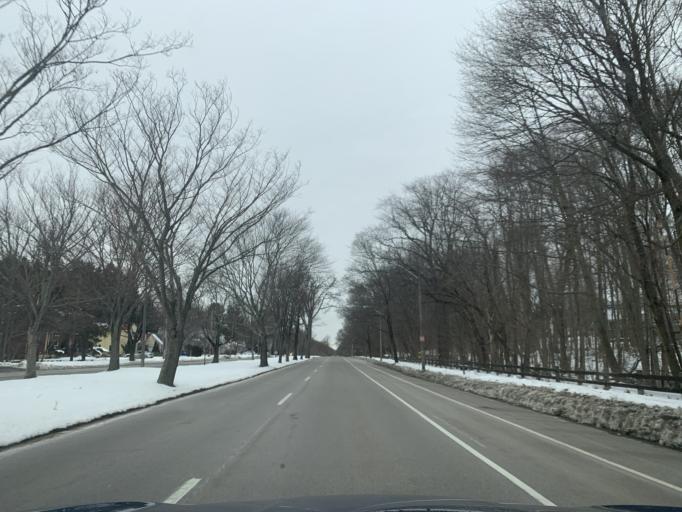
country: US
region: Massachusetts
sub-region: Norfolk County
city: Milton
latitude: 42.2472
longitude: -71.0935
